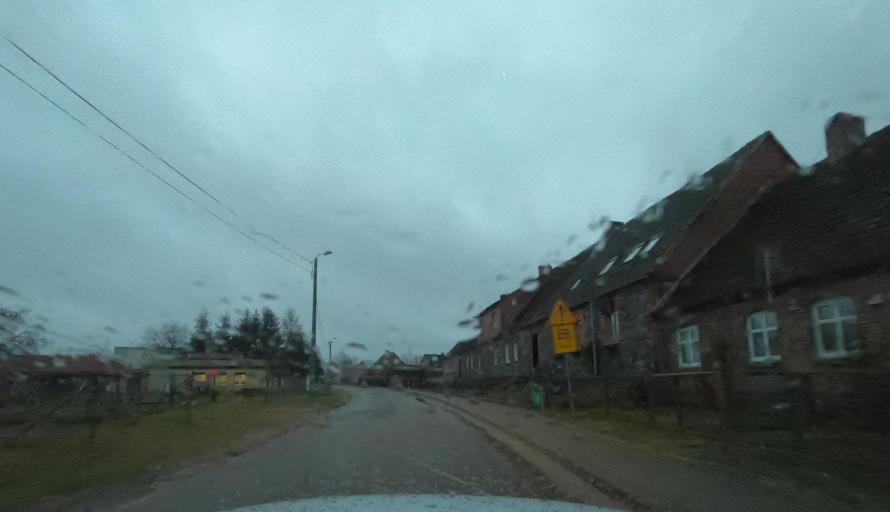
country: PL
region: West Pomeranian Voivodeship
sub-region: Powiat szczecinecki
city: Borne Sulinowo
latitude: 53.6729
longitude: 16.4905
